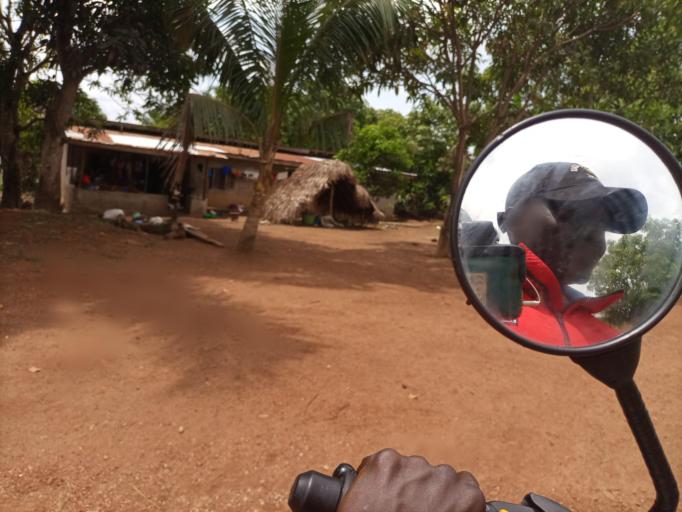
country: SL
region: Southern Province
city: Baoma
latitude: 7.9723
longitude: -11.7136
